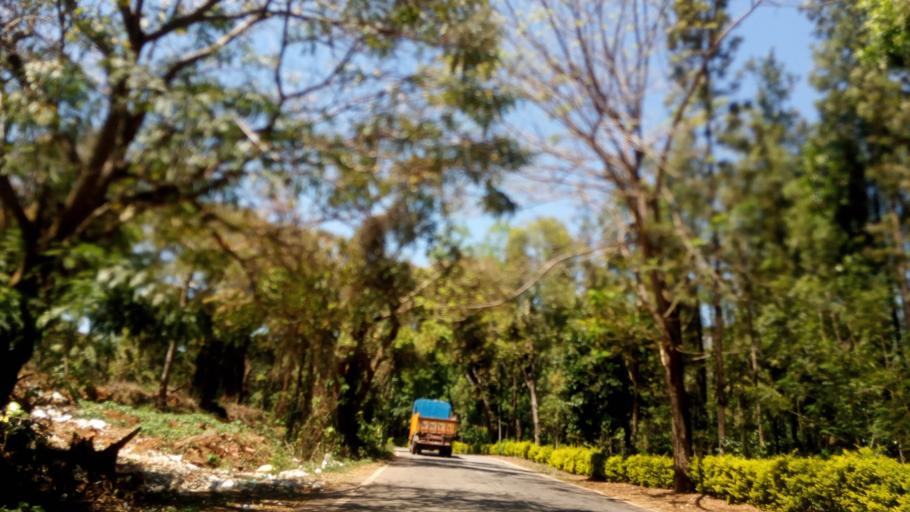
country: IN
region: Karnataka
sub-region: Chikmagalur
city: Chikmagalur
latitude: 13.3802
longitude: 75.7502
